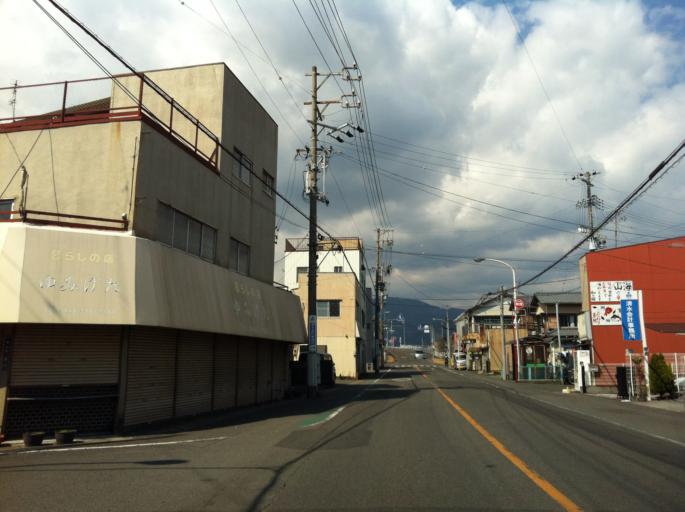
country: JP
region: Shizuoka
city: Shizuoka-shi
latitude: 35.0036
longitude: 138.3636
